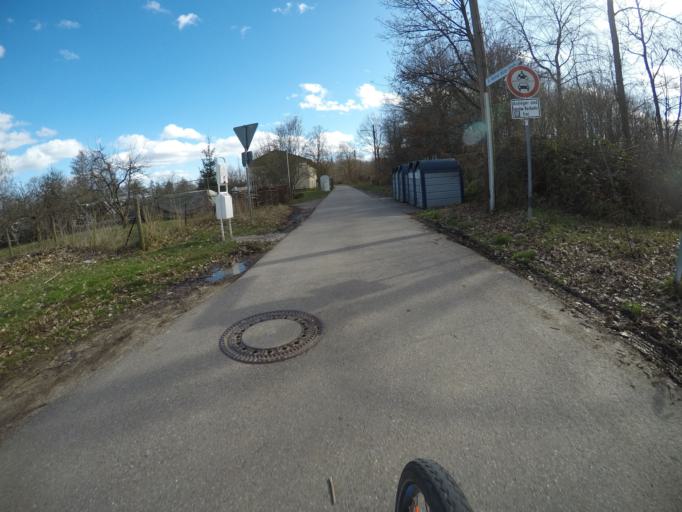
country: DE
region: Baden-Wuerttemberg
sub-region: Regierungsbezirk Stuttgart
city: Leinfelden-Echterdingen
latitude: 48.6632
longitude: 9.1753
